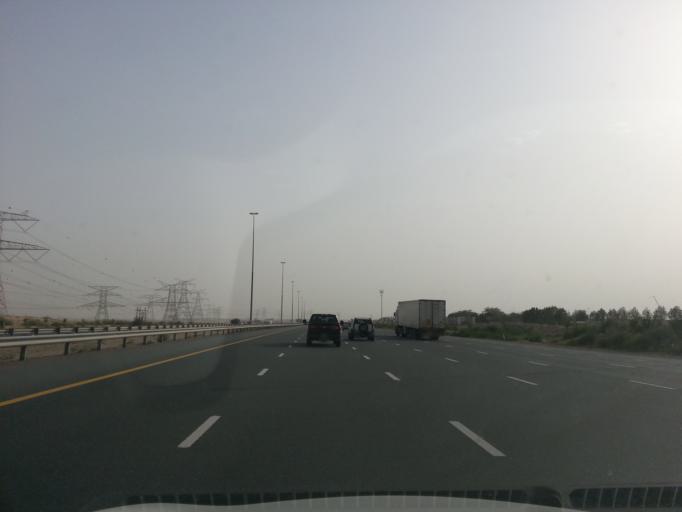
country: AE
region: Dubai
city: Dubai
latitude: 24.9989
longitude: 55.2560
